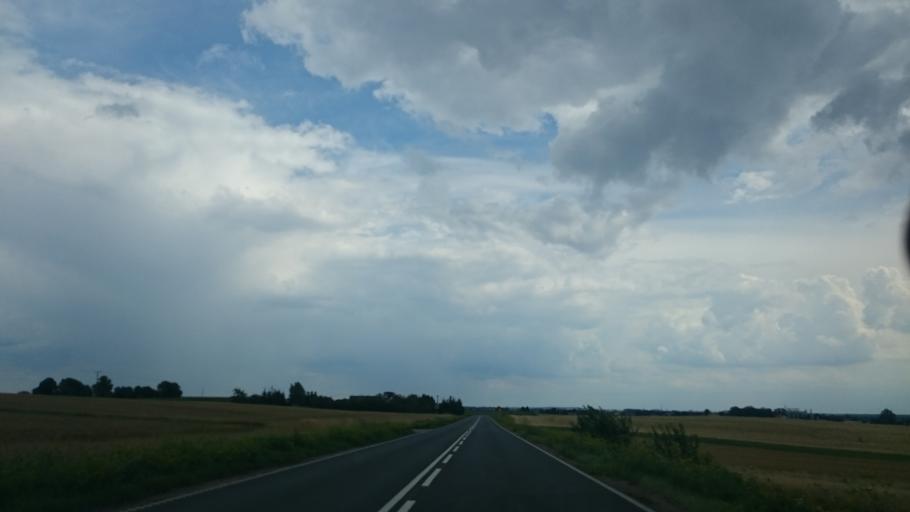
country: PL
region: Kujawsko-Pomorskie
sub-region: Powiat tucholski
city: Kesowo
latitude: 53.6618
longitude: 17.6768
